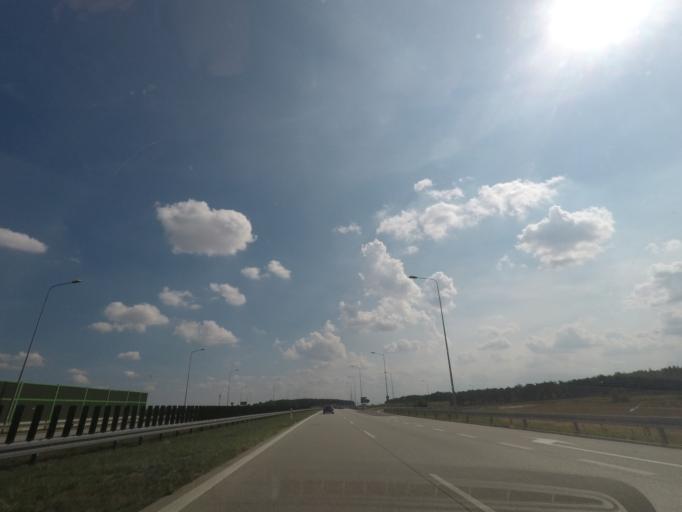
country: PL
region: Lodz Voivodeship
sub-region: Powiat piotrkowski
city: Czarnocin
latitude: 51.5526
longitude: 19.6044
